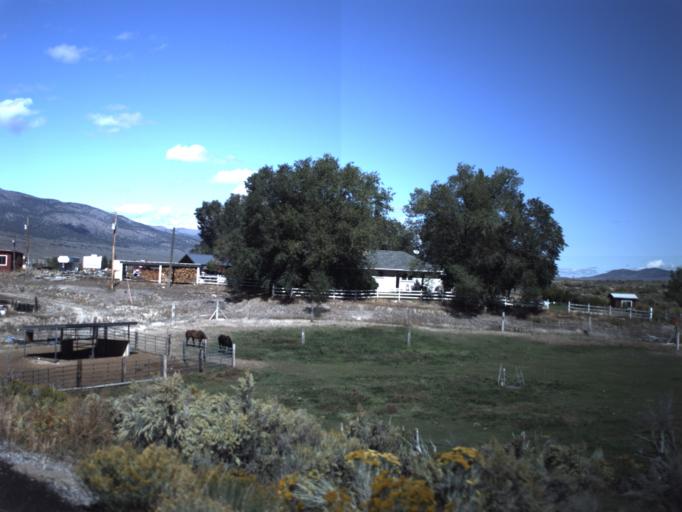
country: US
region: Utah
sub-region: Piute County
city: Junction
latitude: 38.1584
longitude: -112.0056
